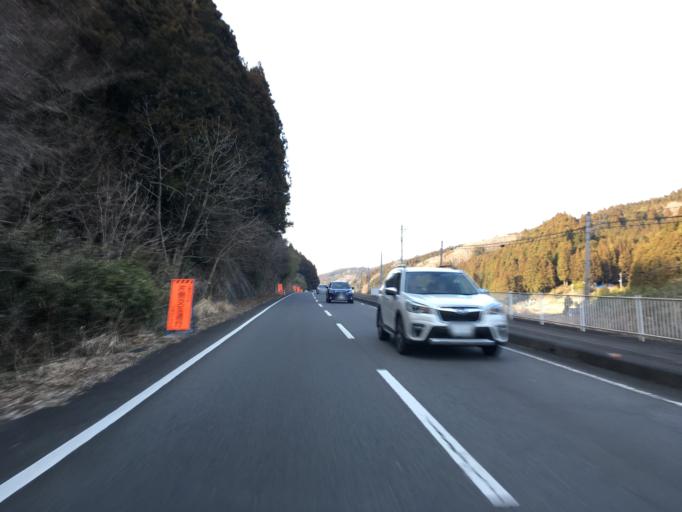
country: JP
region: Ibaraki
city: Daigo
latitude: 36.7251
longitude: 140.4600
